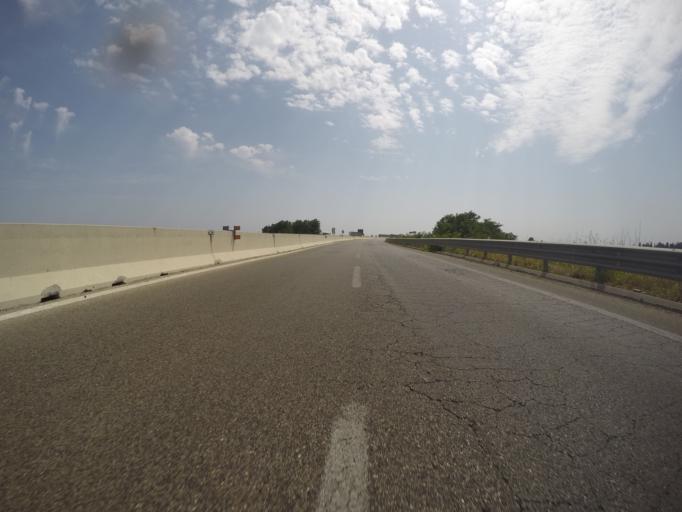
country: IT
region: Apulia
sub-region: Provincia di Brindisi
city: Mesagne
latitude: 40.5710
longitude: 17.8087
